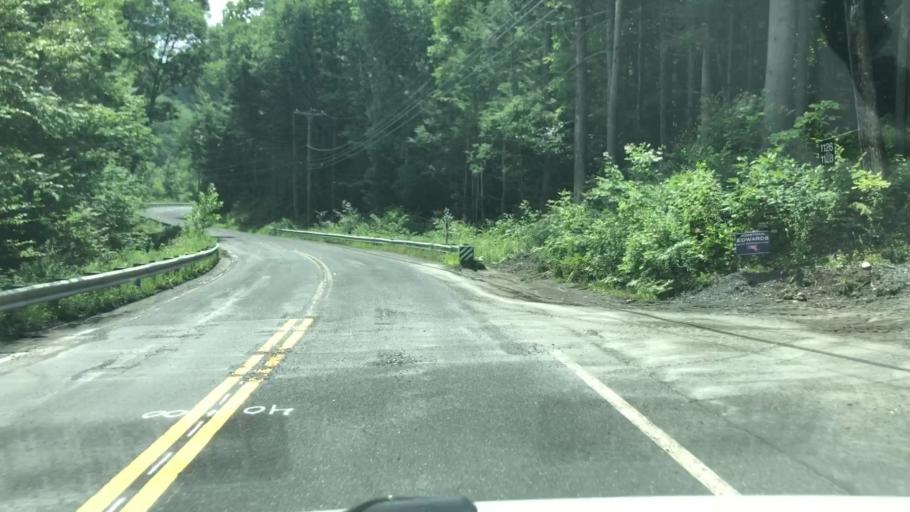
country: US
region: Massachusetts
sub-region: Franklin County
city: Conway
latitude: 42.5157
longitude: -72.7372
